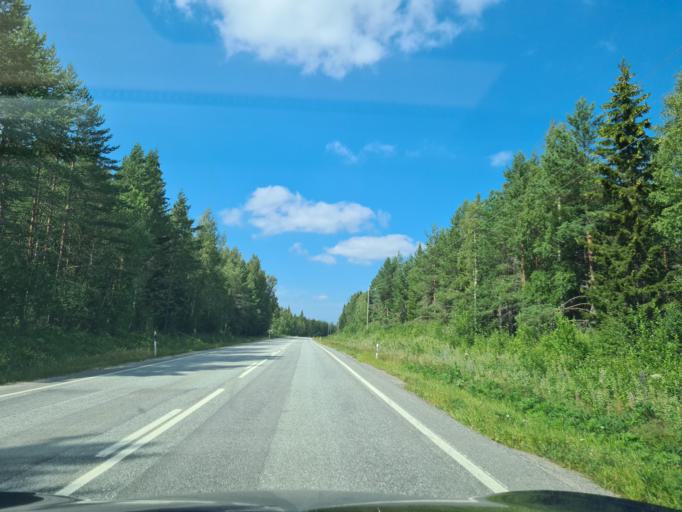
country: FI
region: Ostrobothnia
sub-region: Vaasa
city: Vaasa
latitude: 63.1809
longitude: 21.5724
